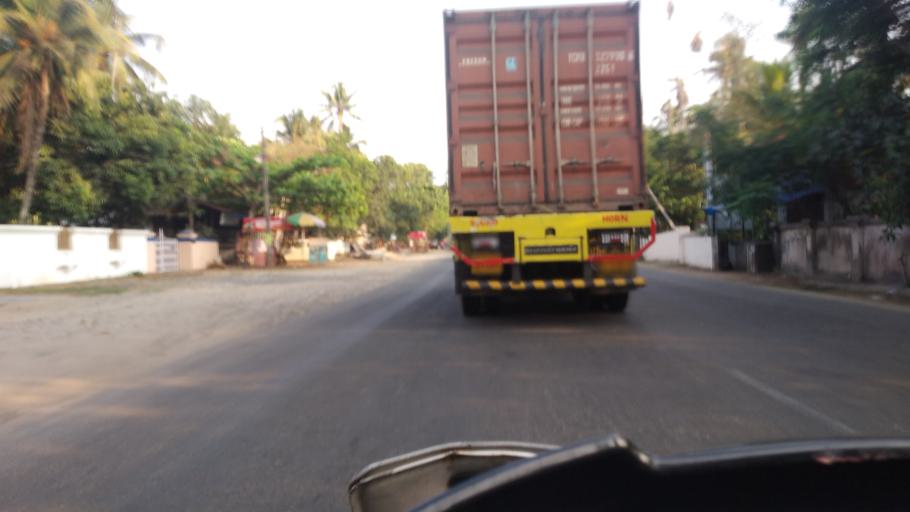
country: IN
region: Kerala
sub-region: Thrissur District
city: Thanniyam
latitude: 10.3921
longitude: 76.1178
